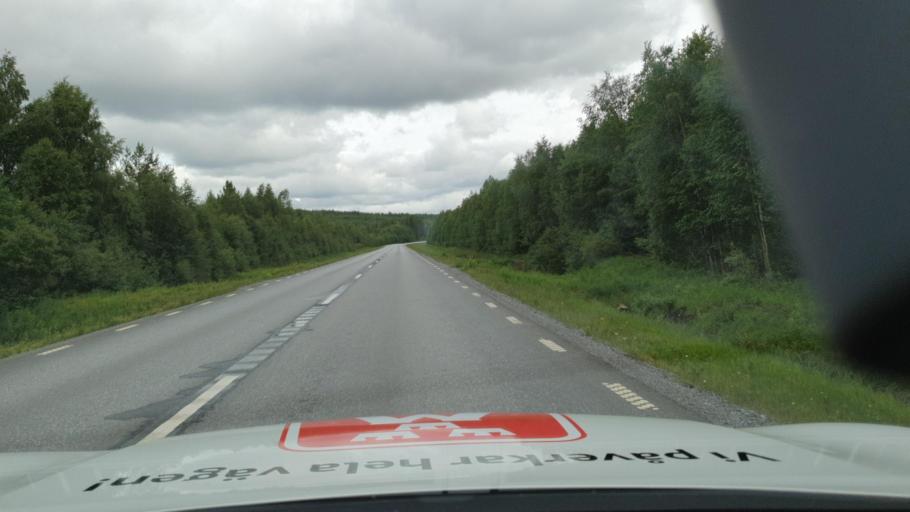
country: SE
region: Vaesterbotten
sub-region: Dorotea Kommun
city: Dorotea
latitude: 64.2970
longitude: 16.5493
